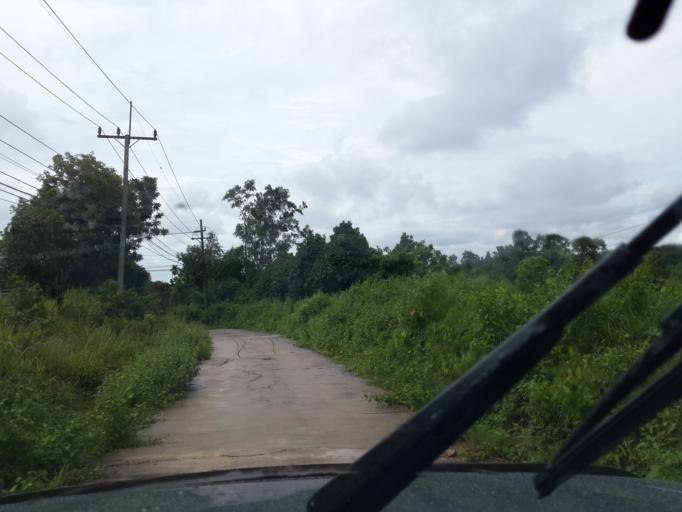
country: TH
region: Narathiwat
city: Rueso
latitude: 6.3806
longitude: 101.5248
